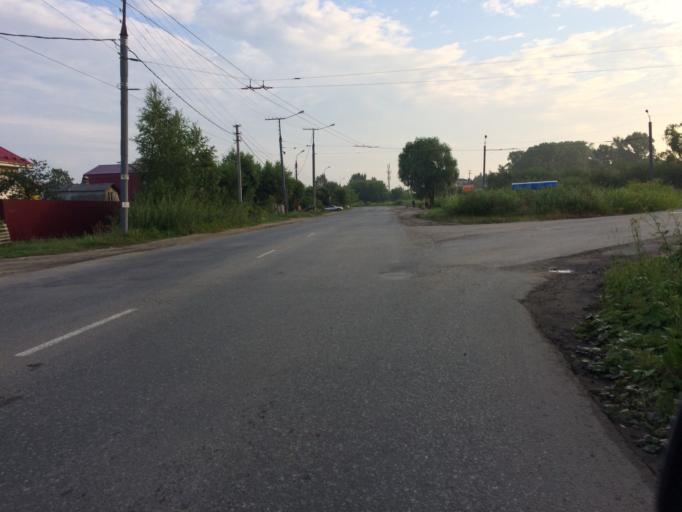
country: RU
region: Mariy-El
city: Yoshkar-Ola
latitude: 56.6456
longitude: 47.9544
